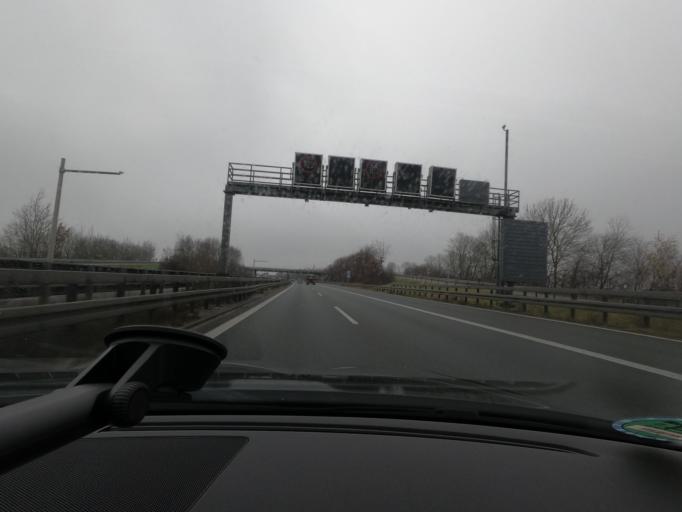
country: DE
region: Bavaria
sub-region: Regierungsbezirk Mittelfranken
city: Bubenreuth
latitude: 49.6383
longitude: 11.0125
